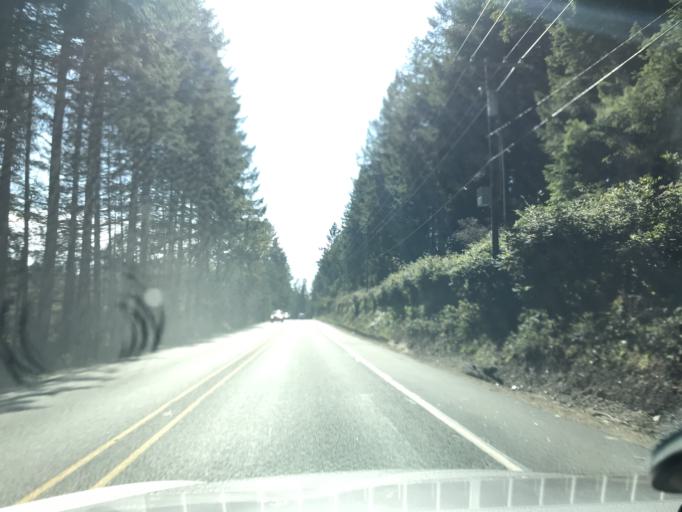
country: US
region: Washington
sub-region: Pierce County
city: Key Center
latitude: 47.3335
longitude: -122.7509
